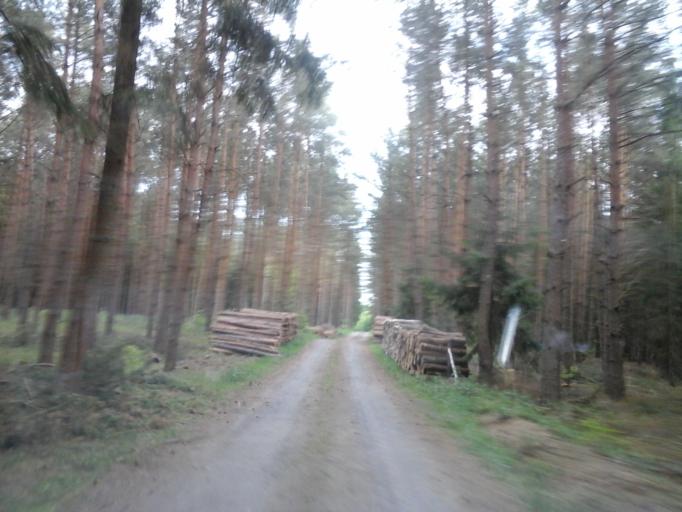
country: PL
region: West Pomeranian Voivodeship
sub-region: Powiat choszczenski
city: Pelczyce
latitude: 52.9565
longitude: 15.3296
